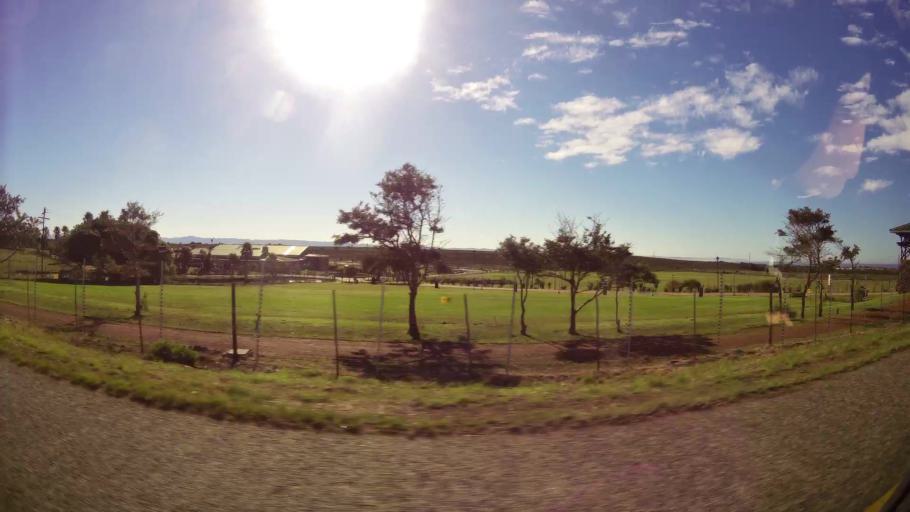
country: ZA
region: Eastern Cape
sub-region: Cacadu District Municipality
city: Jeffrey's Bay
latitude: -34.0186
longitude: 24.8902
